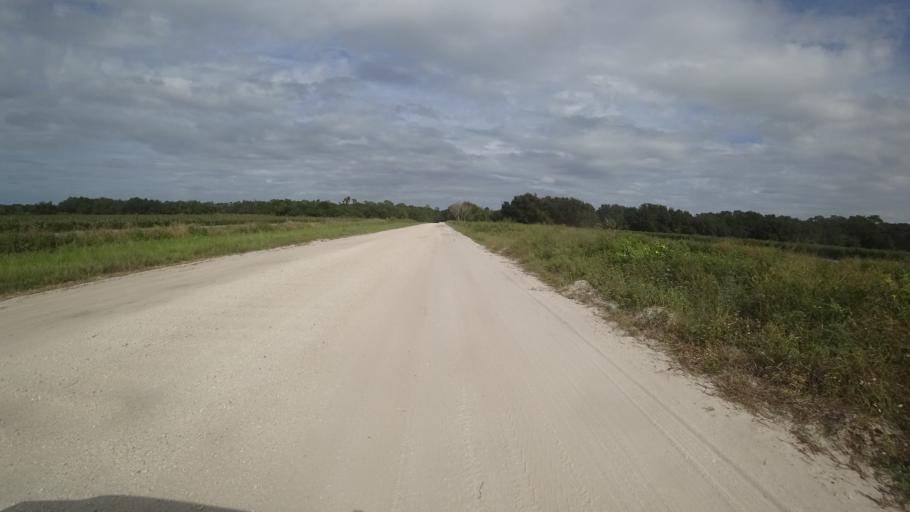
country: US
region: Florida
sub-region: Hillsborough County
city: Wimauma
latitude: 27.5954
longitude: -82.3113
